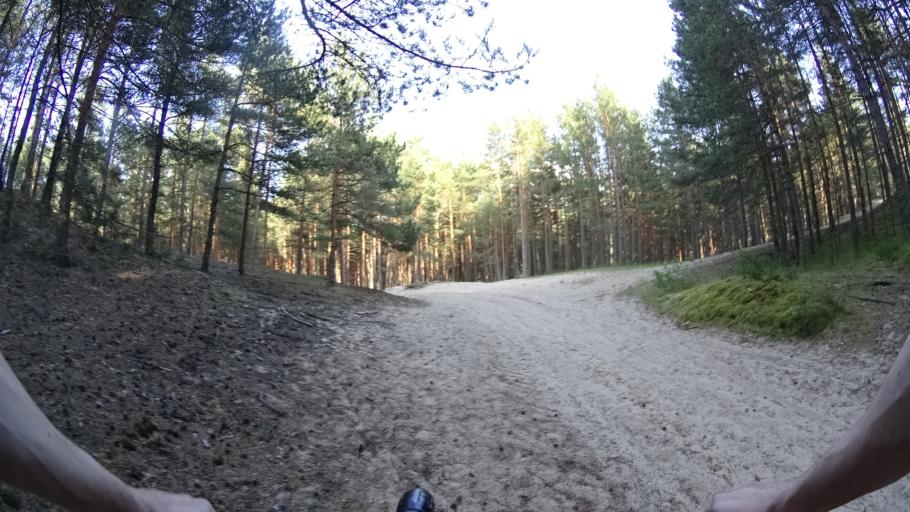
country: LV
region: Riga
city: Jaunciems
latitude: 57.0868
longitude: 24.1407
